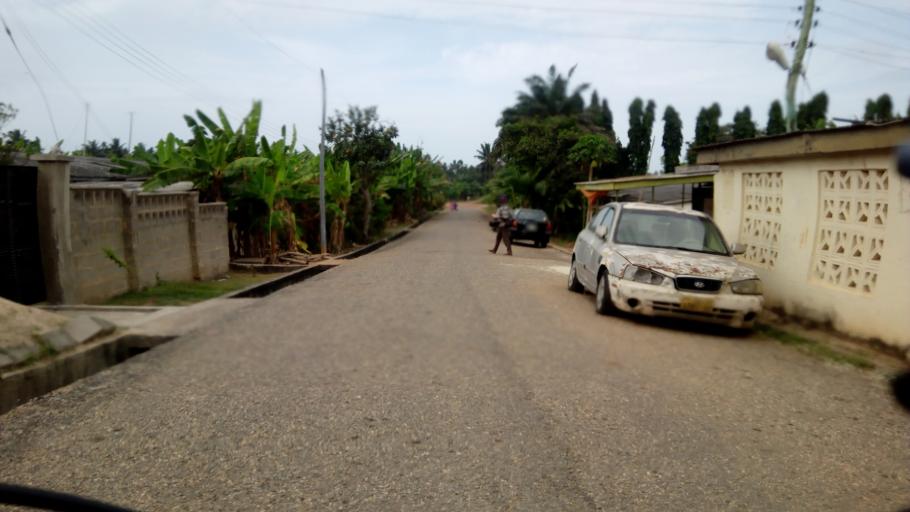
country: GH
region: Central
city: Cape Coast
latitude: 5.1043
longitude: -1.2787
